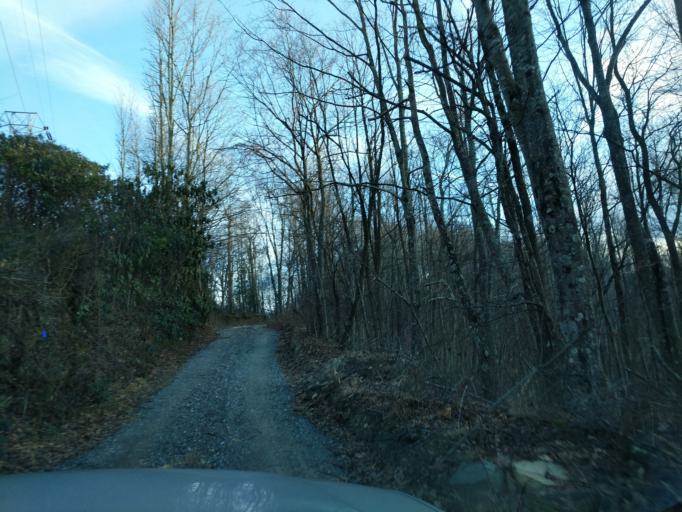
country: US
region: North Carolina
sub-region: Haywood County
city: Cove Creek
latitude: 35.7299
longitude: -83.0541
